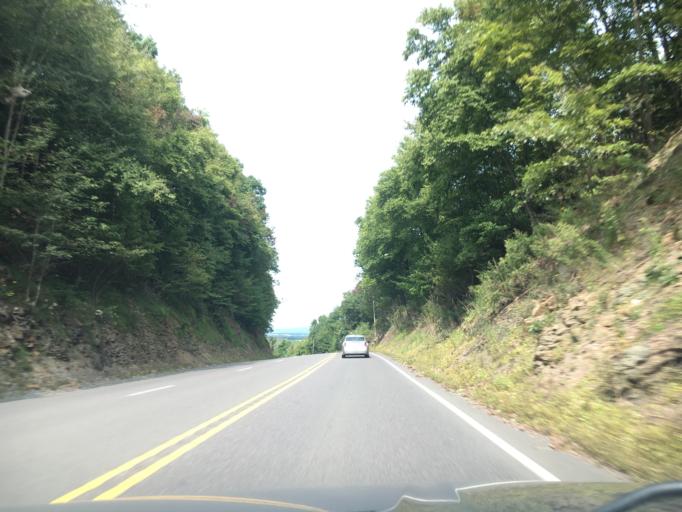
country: US
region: Pennsylvania
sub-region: Carbon County
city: Summit Hill
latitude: 40.7101
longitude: -75.8288
